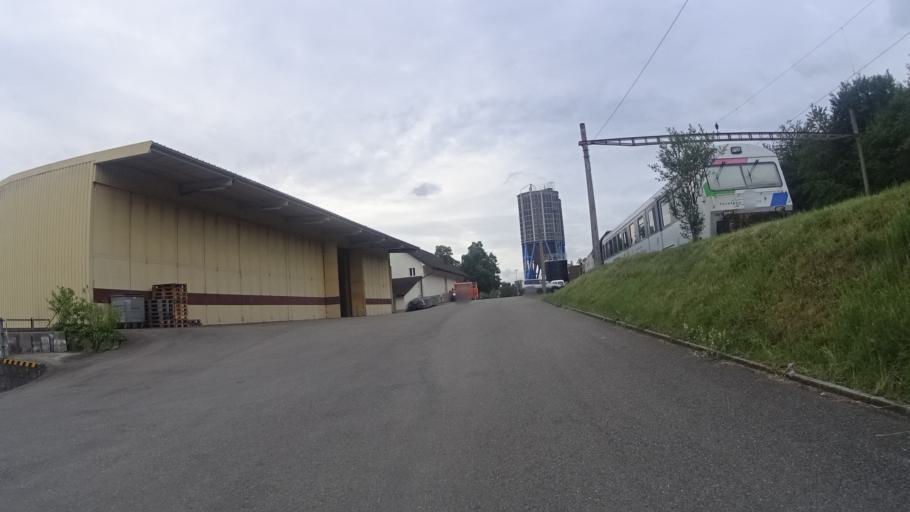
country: DE
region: Baden-Wuerttemberg
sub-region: Freiburg Region
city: Waldshut-Tiengen
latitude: 47.6072
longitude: 8.2209
